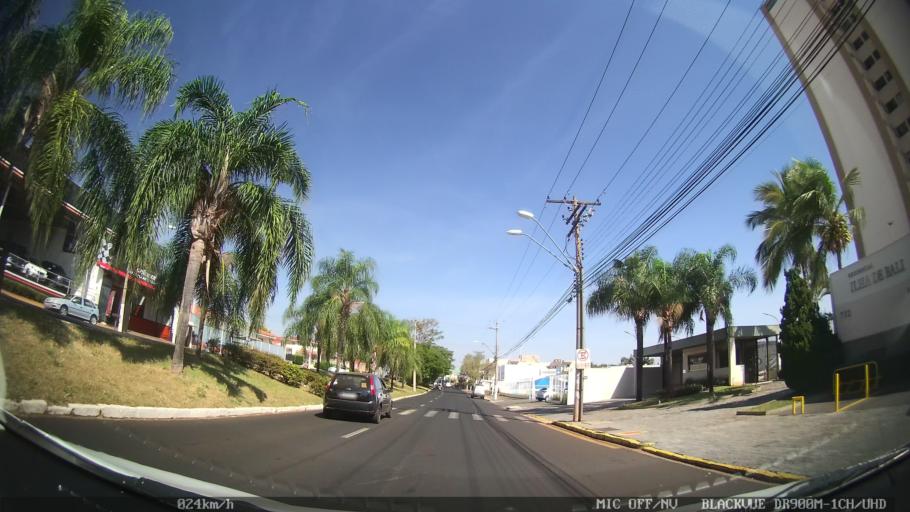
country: BR
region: Sao Paulo
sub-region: Ribeirao Preto
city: Ribeirao Preto
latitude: -21.1846
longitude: -47.8190
